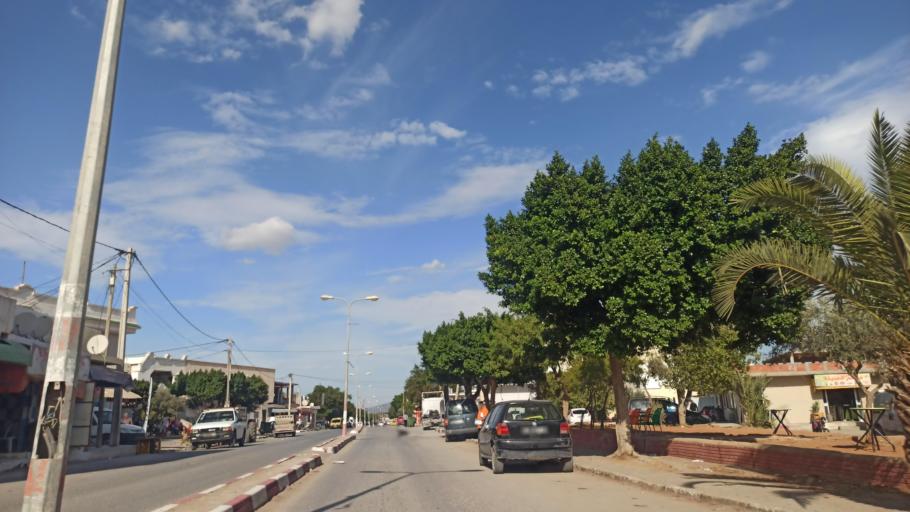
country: TN
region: Zaghwan
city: Zaghouan
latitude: 36.3524
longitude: 10.2089
